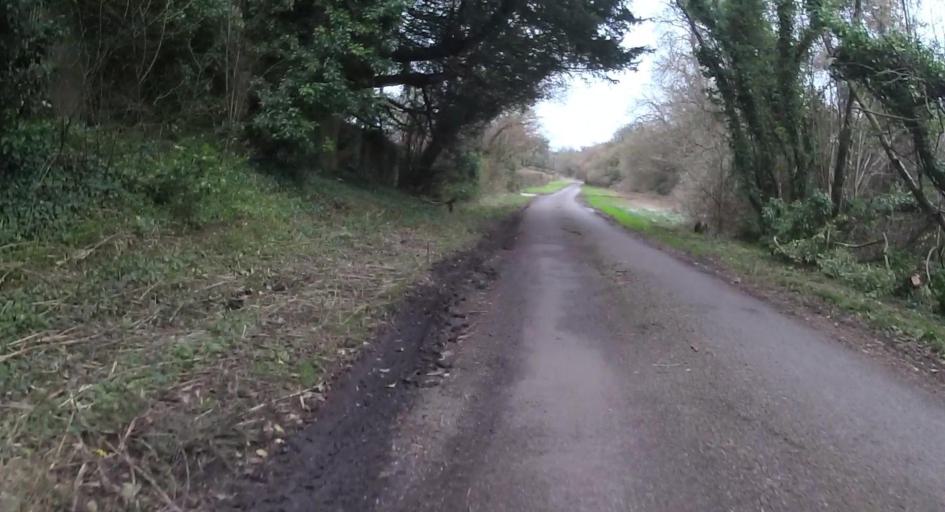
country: GB
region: England
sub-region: Hampshire
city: Highclere
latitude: 51.3286
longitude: -1.3183
